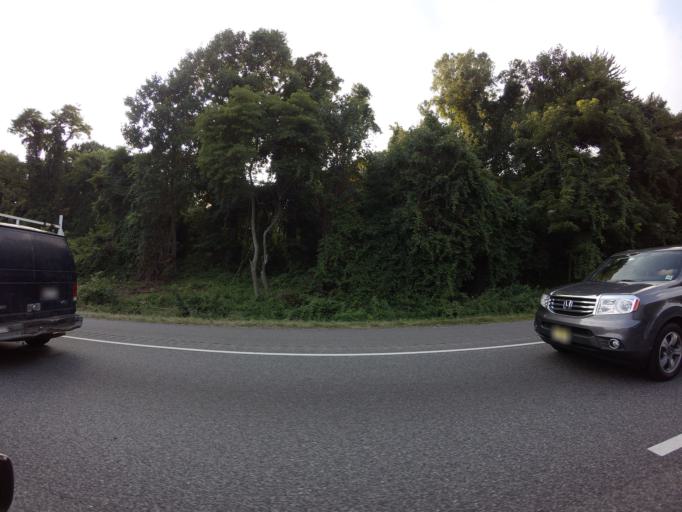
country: US
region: Maryland
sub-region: Howard County
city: Savage
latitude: 39.1532
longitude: -76.8385
